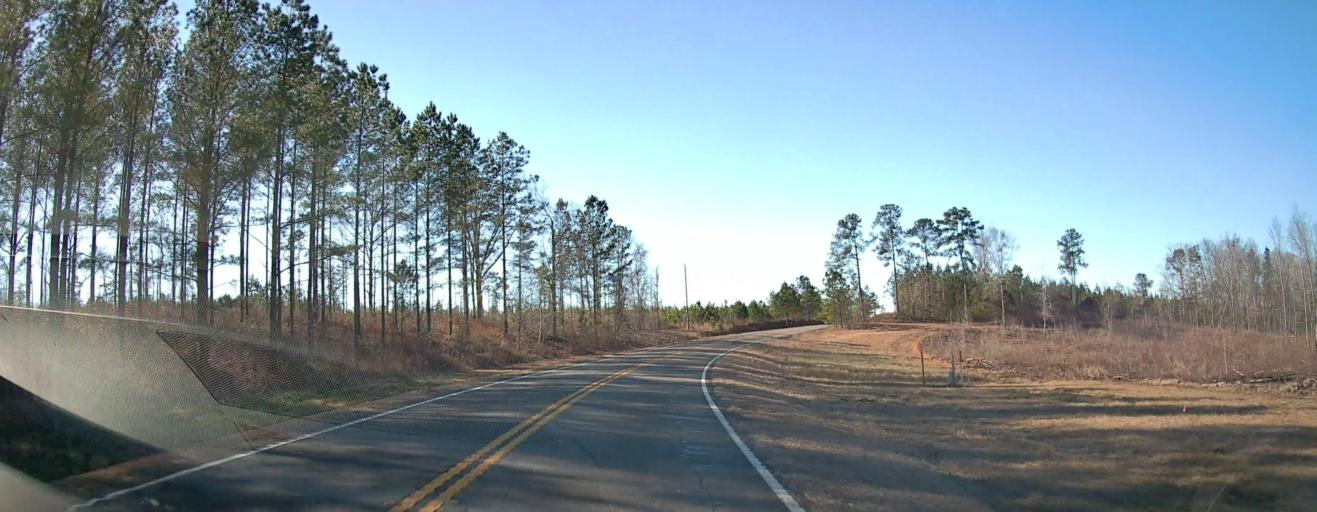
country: US
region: Georgia
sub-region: Talbot County
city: Talbotton
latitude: 32.6476
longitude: -84.3873
